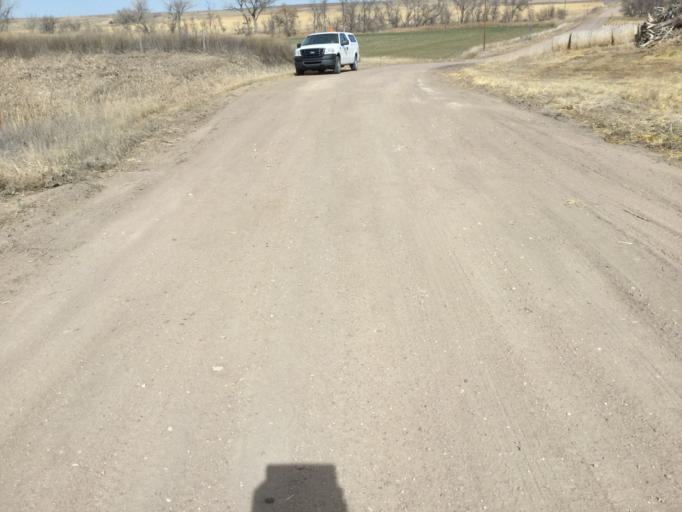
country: US
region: Kansas
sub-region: Rawlins County
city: Atwood
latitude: 39.8615
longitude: -100.9076
